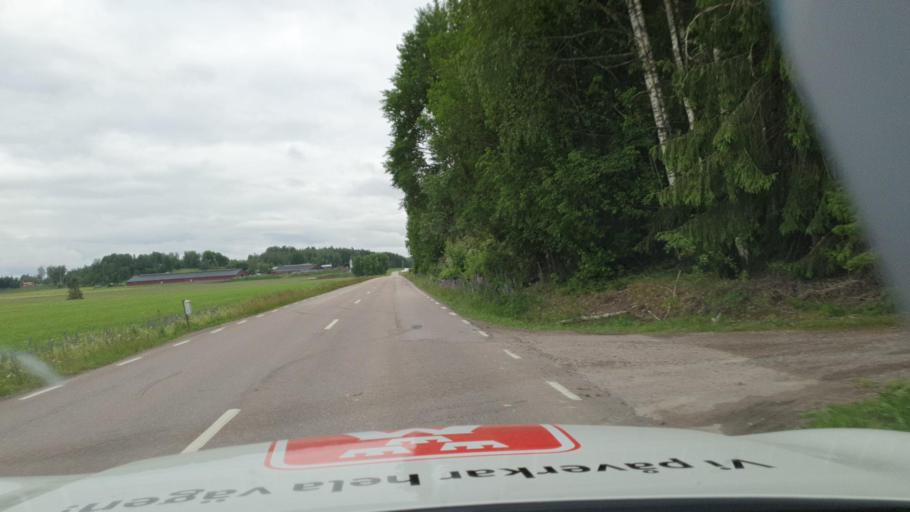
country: SE
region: Vaermland
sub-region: Kils Kommun
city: Kil
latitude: 59.5667
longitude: 13.2918
